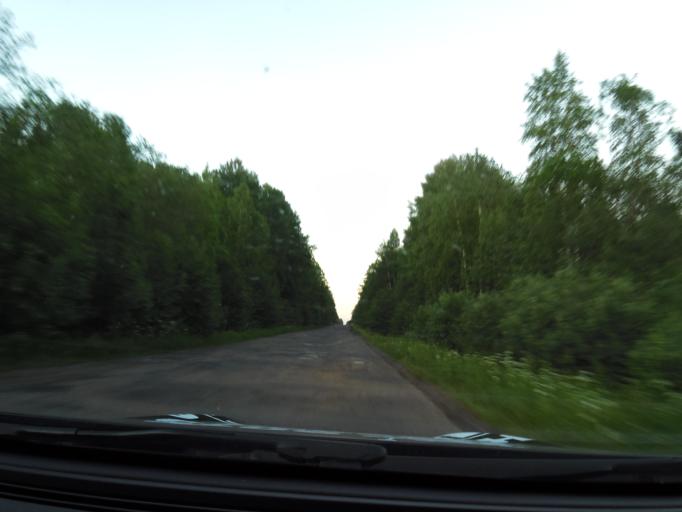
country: RU
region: Leningrad
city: Voznesen'ye
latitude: 60.8353
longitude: 35.6644
